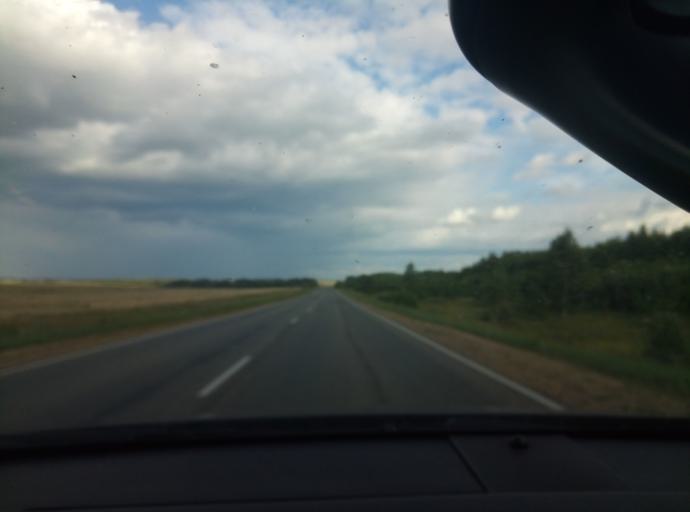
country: RU
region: Kaluga
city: Nikola-Lenivets
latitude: 54.5325
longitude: 35.5670
